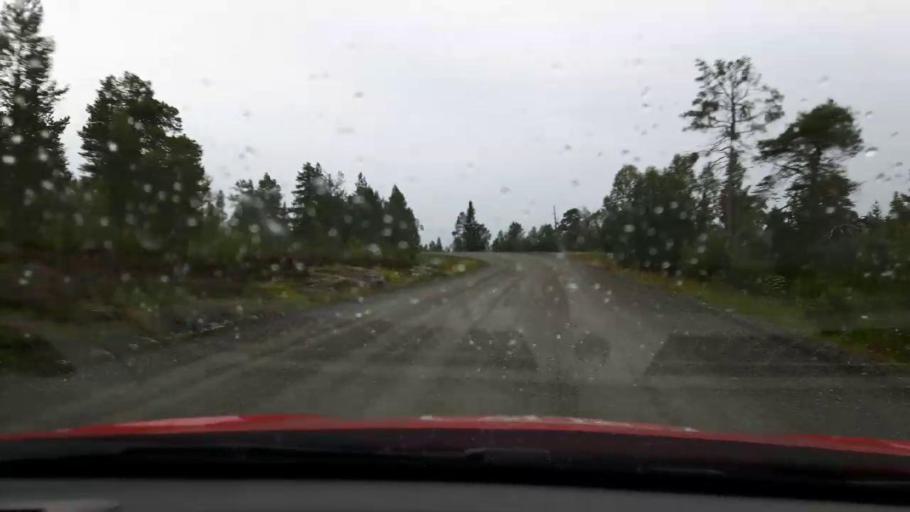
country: NO
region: Nord-Trondelag
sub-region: Meraker
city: Meraker
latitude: 63.6408
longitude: 12.2738
